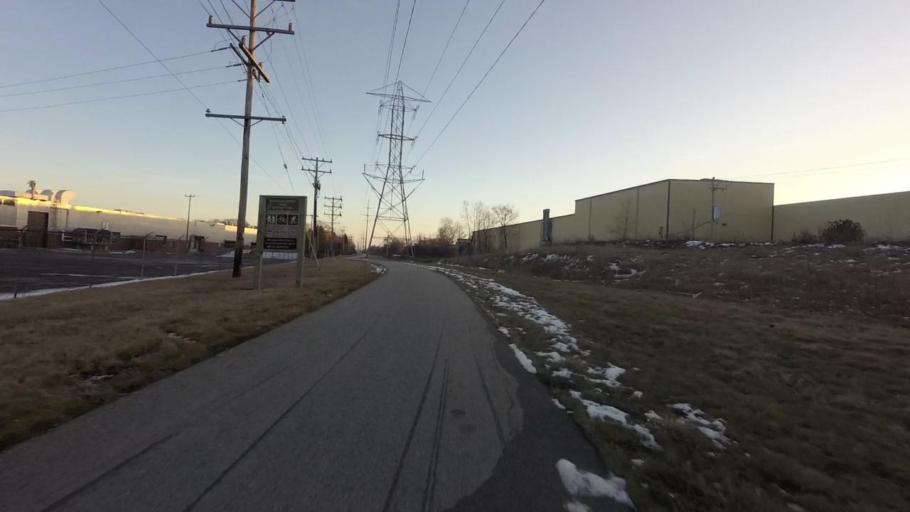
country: US
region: Wisconsin
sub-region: Milwaukee County
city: Brown Deer
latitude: 43.1477
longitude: -87.9540
